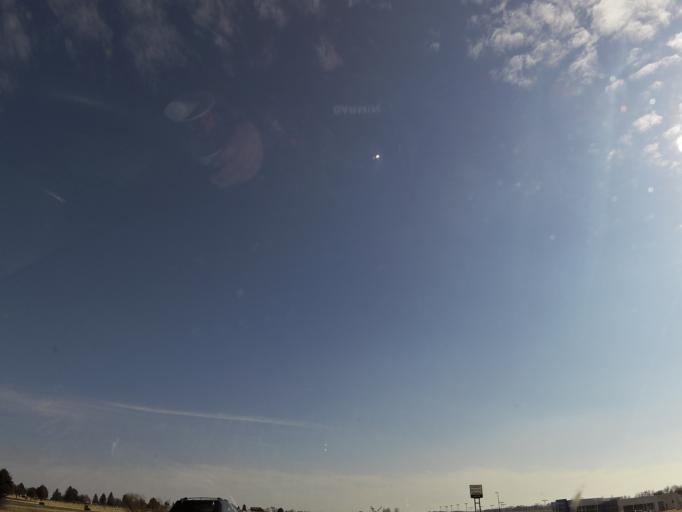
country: US
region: Minnesota
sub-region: Steele County
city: Medford
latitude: 44.1308
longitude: -93.2479
